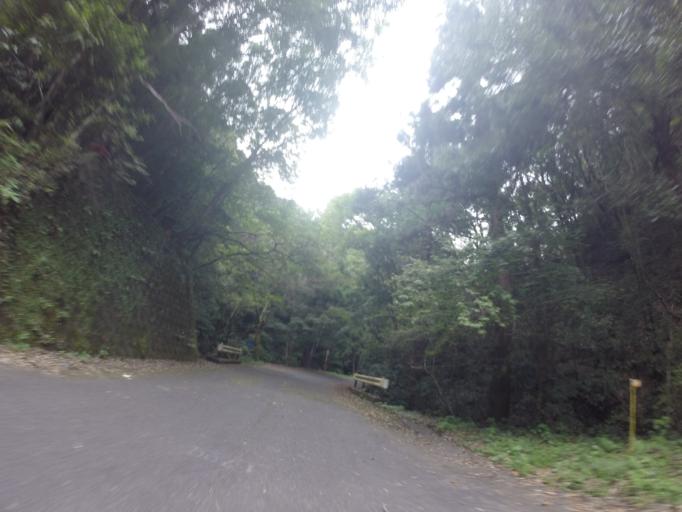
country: JP
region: Shizuoka
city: Fujieda
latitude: 34.9209
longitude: 138.2258
